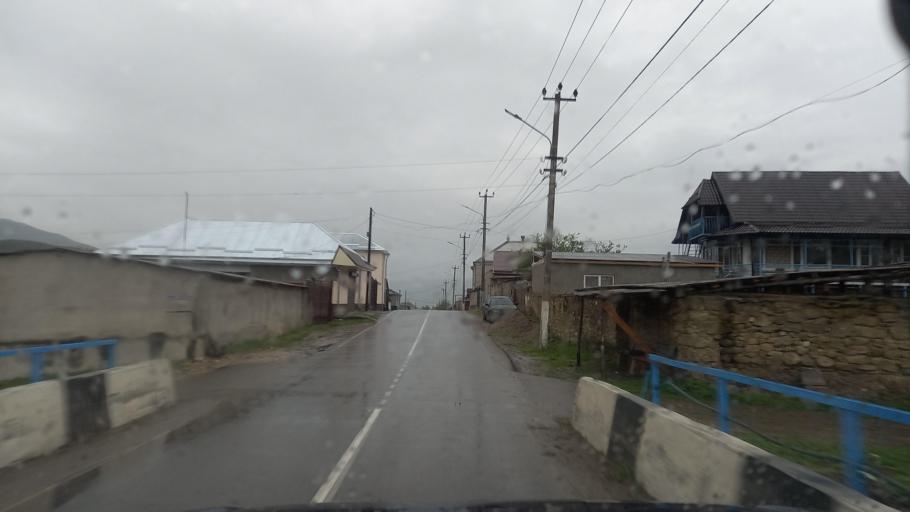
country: RU
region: Kabardino-Balkariya
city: Gundelen
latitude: 43.5951
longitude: 43.1750
